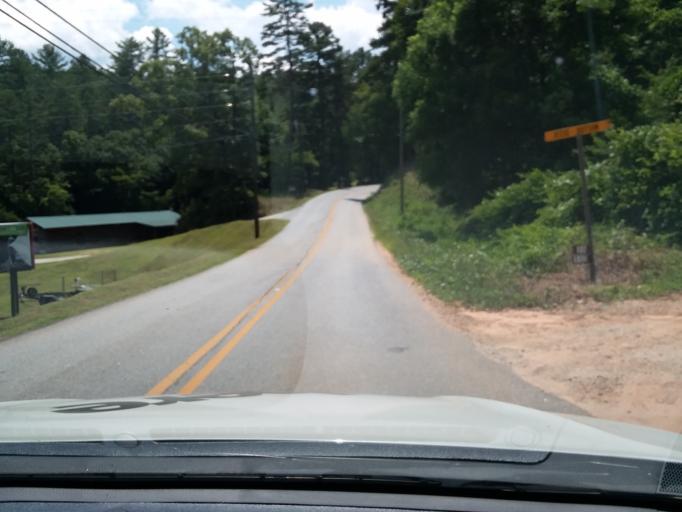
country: US
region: Georgia
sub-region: Rabun County
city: Clayton
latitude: 34.7768
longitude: -83.4174
